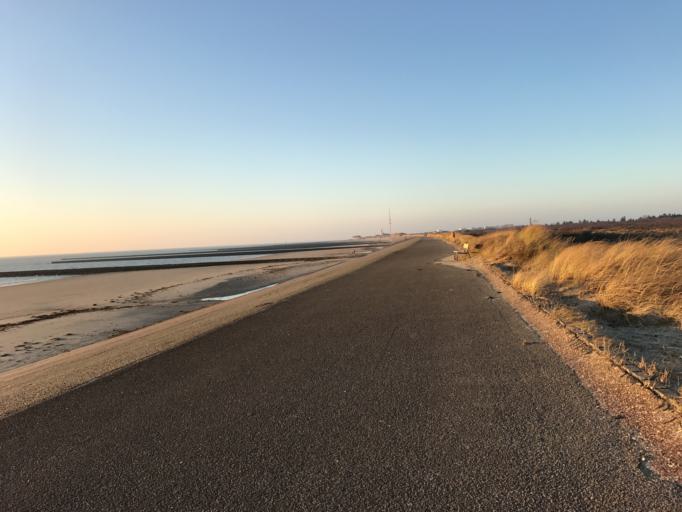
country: DE
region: Lower Saxony
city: Borkum
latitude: 53.5689
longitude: 6.6918
